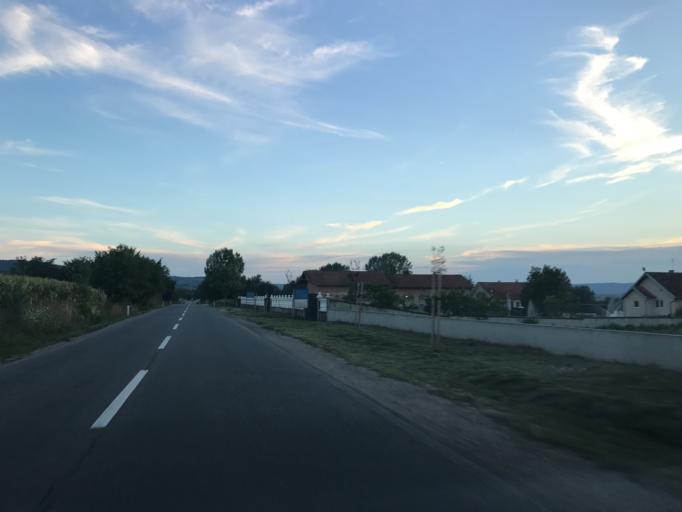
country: RS
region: Central Serbia
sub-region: Branicevski Okrug
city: Veliko Gradiste
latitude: 44.7494
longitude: 21.4929
